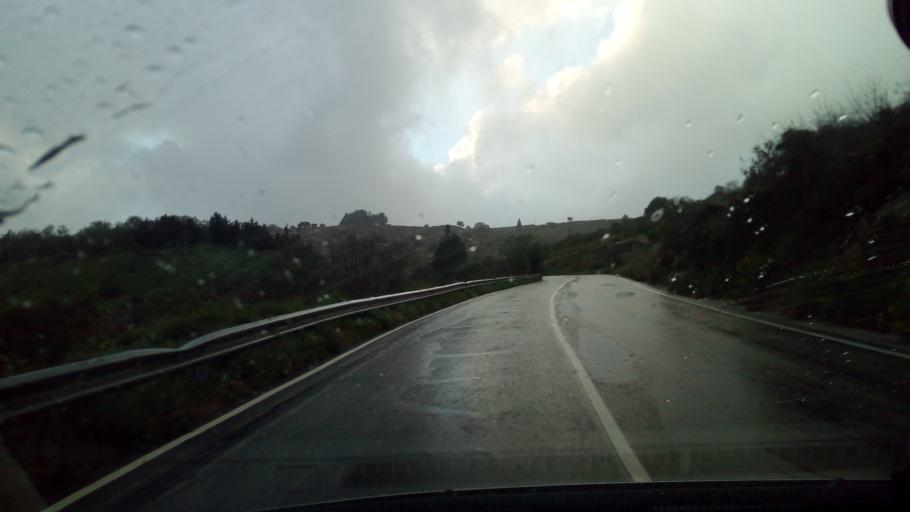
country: CY
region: Pafos
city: Pegeia
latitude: 34.9547
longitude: 32.4172
